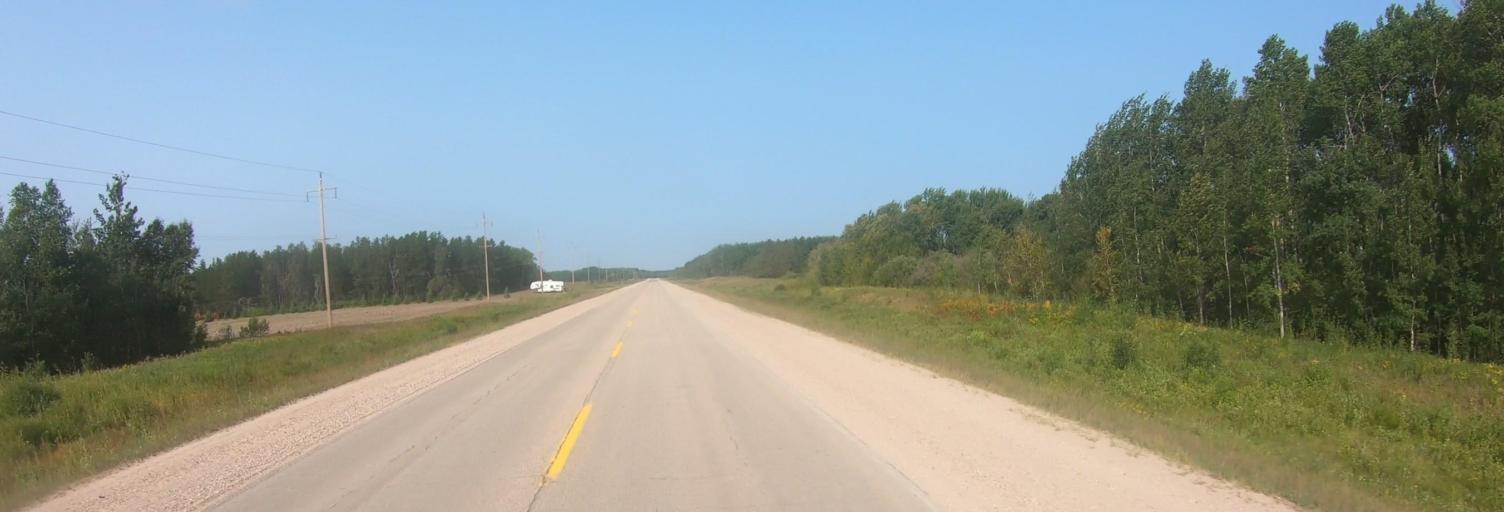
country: US
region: Minnesota
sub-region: Roseau County
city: Roseau
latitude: 49.0234
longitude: -95.7161
